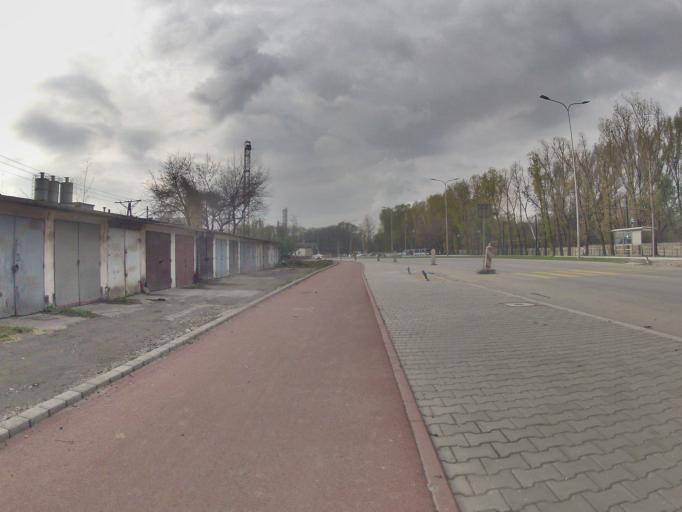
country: PL
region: Lesser Poland Voivodeship
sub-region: Powiat wielicki
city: Wegrzce Wielkie
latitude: 50.0696
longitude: 20.0953
